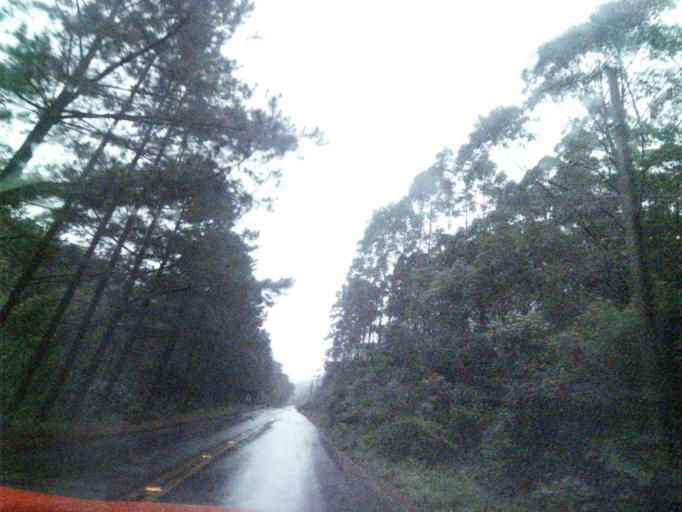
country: BR
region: Santa Catarina
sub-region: Anitapolis
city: Anitapolis
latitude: -27.7837
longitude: -49.0429
